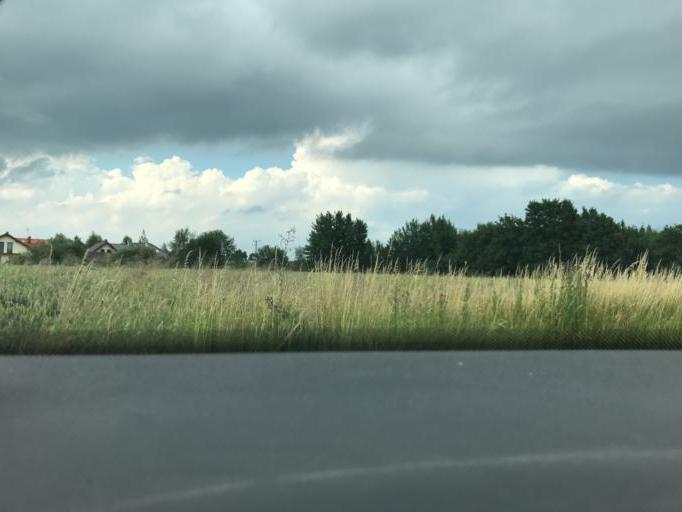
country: PL
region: Pomeranian Voivodeship
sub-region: Powiat gdanski
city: Cedry Wielkie
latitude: 54.3343
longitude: 18.8046
